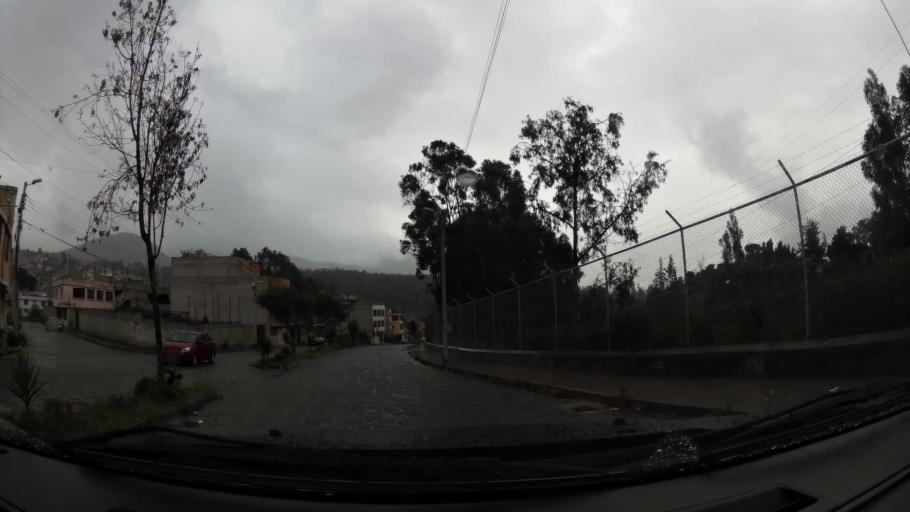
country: EC
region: Pichincha
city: Quito
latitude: -0.0964
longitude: -78.4992
